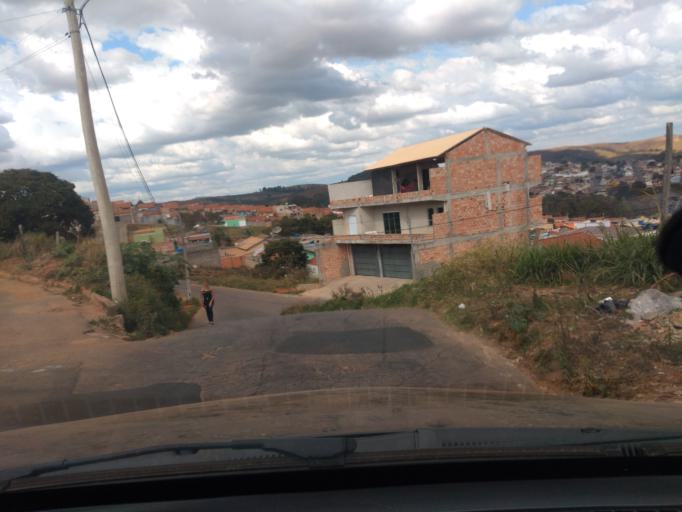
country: BR
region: Minas Gerais
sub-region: Tres Coracoes
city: Tres Coracoes
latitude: -21.6948
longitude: -45.2413
